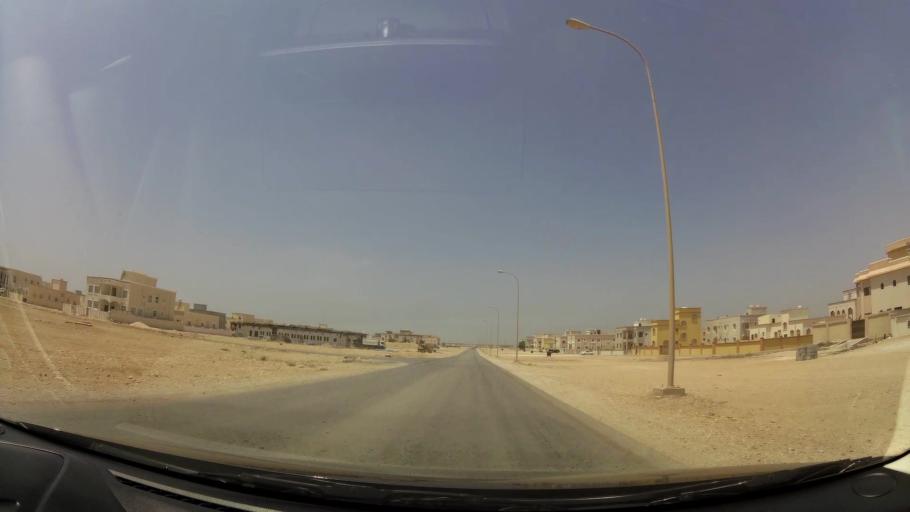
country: OM
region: Zufar
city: Salalah
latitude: 17.0741
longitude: 54.2054
